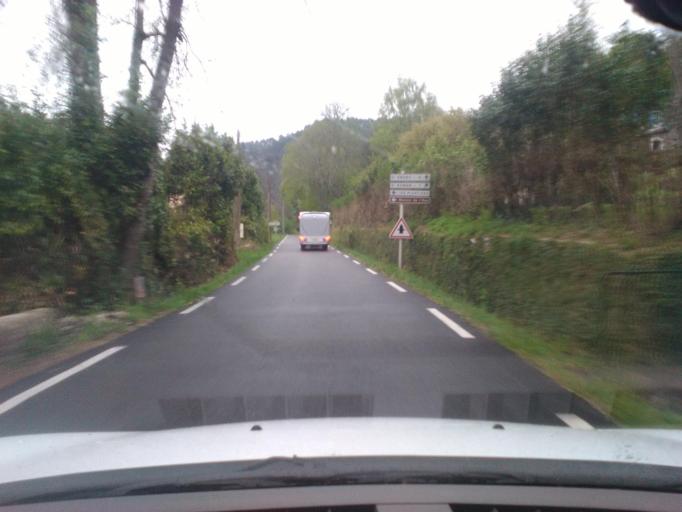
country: FR
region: Languedoc-Roussillon
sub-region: Departement du Gard
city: Lasalle
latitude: 44.1249
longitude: 3.7639
